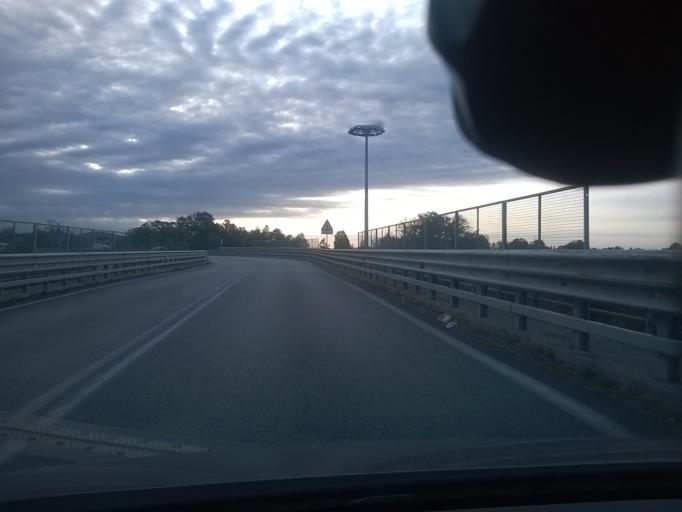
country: IT
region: Lombardy
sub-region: Provincia di Bergamo
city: Grassobbio
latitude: 45.6655
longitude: 9.7377
